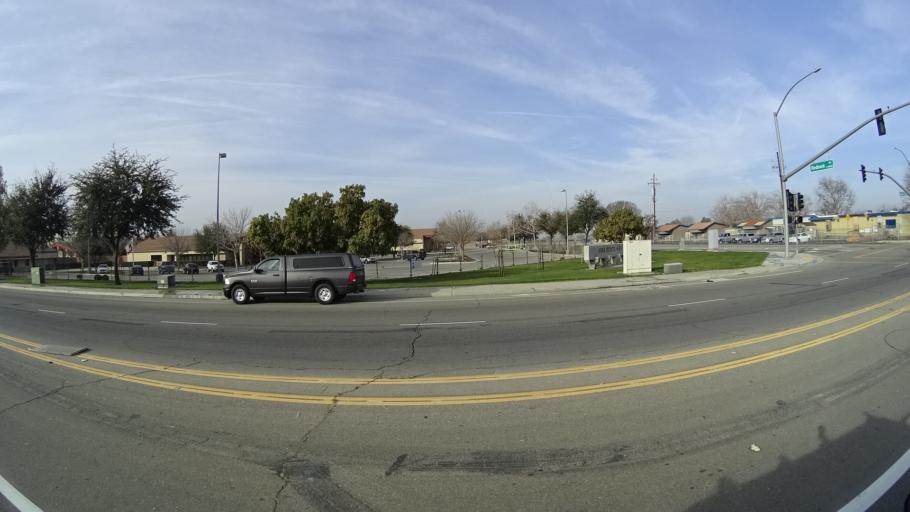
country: US
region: California
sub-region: Kern County
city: Lamont
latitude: 35.3393
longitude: -118.9320
